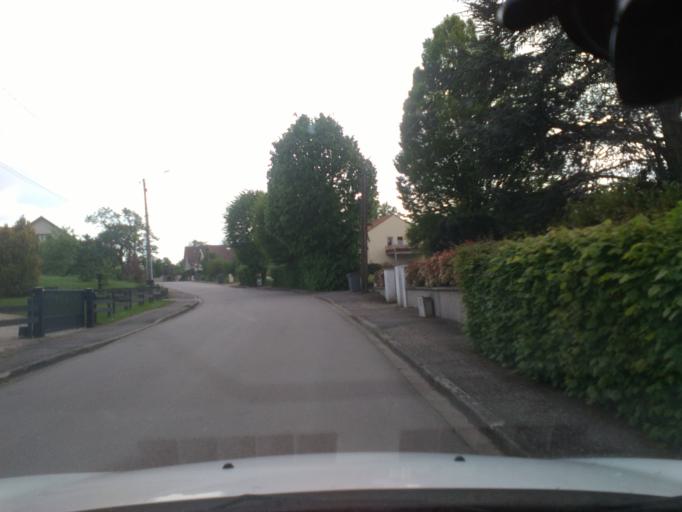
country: FR
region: Lorraine
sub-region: Departement des Vosges
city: Mirecourt
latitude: 48.3047
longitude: 6.1413
